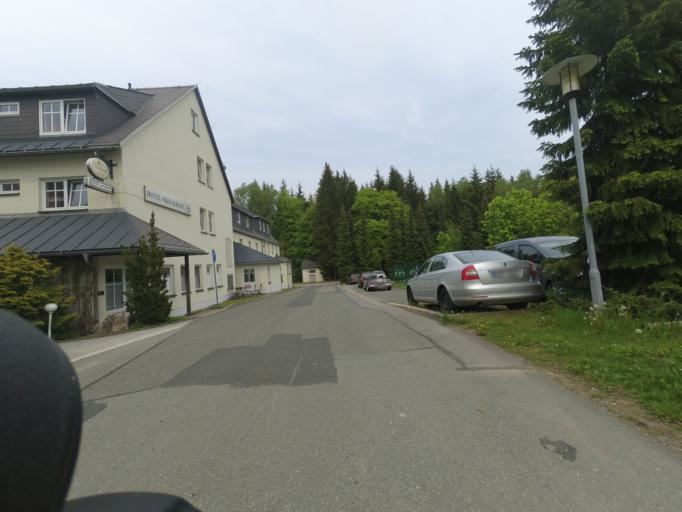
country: DE
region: Saxony
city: Grossruckerswalde
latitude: 50.6567
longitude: 13.1243
